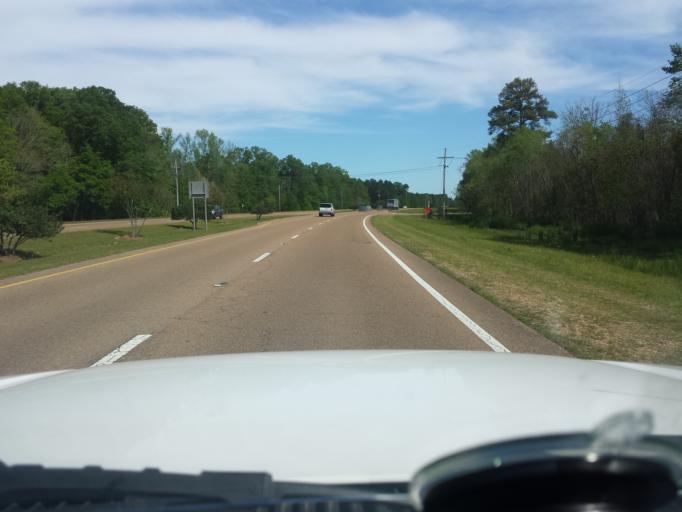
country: US
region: Mississippi
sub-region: Rankin County
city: Flowood
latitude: 32.3187
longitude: -90.0912
